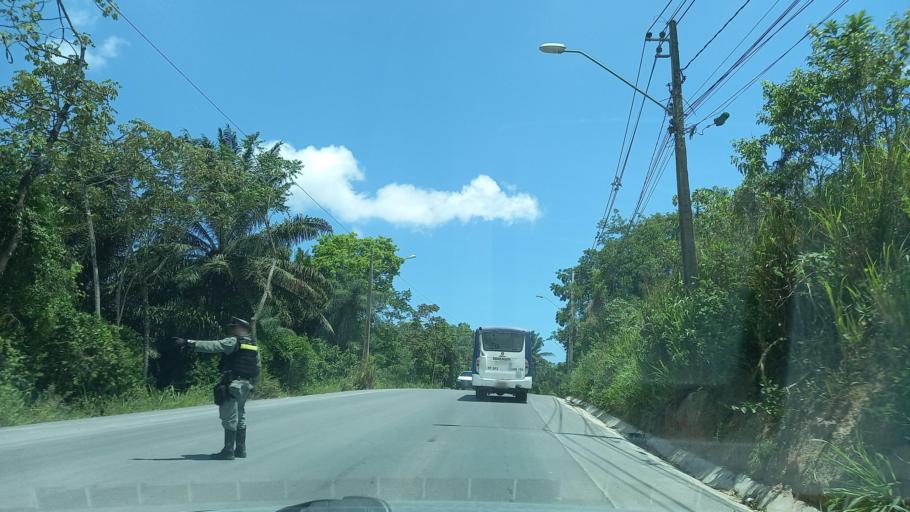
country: BR
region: Pernambuco
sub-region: Jaboatao Dos Guararapes
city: Jaboatao
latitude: -8.1606
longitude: -34.9866
